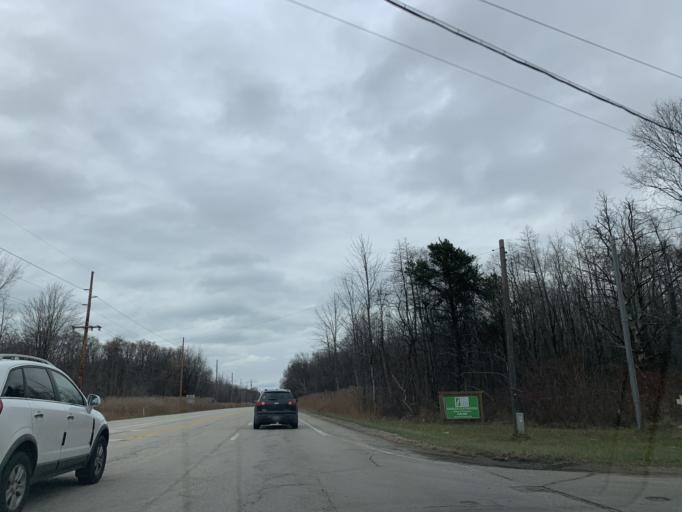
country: US
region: Indiana
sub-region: LaPorte County
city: Long Beach
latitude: 41.7236
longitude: -86.8260
